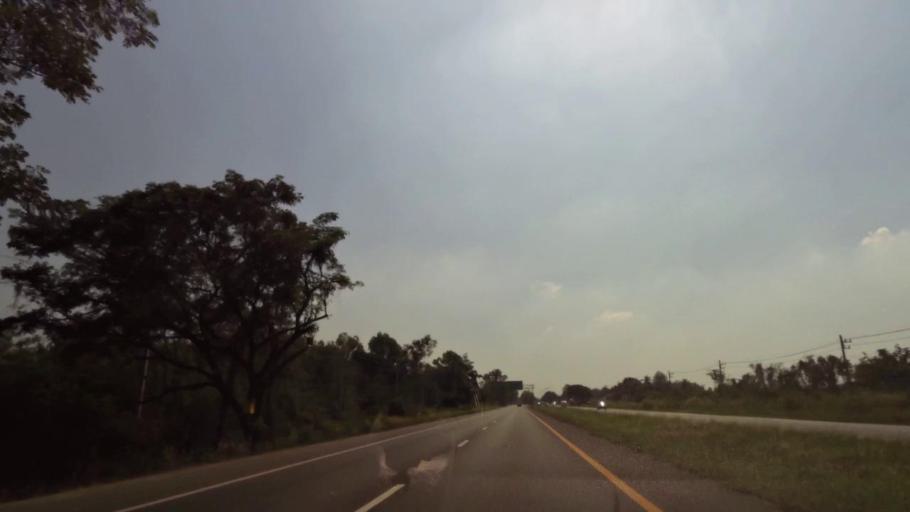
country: TH
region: Phichit
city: Bueng Na Rang
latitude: 16.1973
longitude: 100.1282
